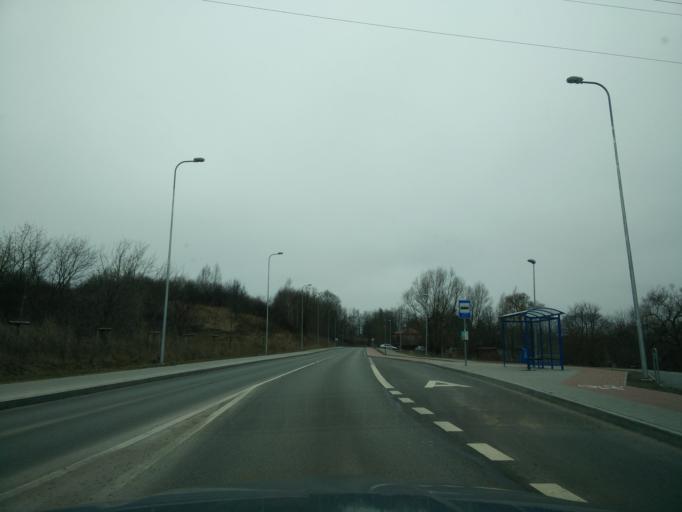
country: LT
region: Klaipedos apskritis
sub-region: Klaipeda
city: Klaipeda
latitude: 55.7178
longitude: 21.1686
